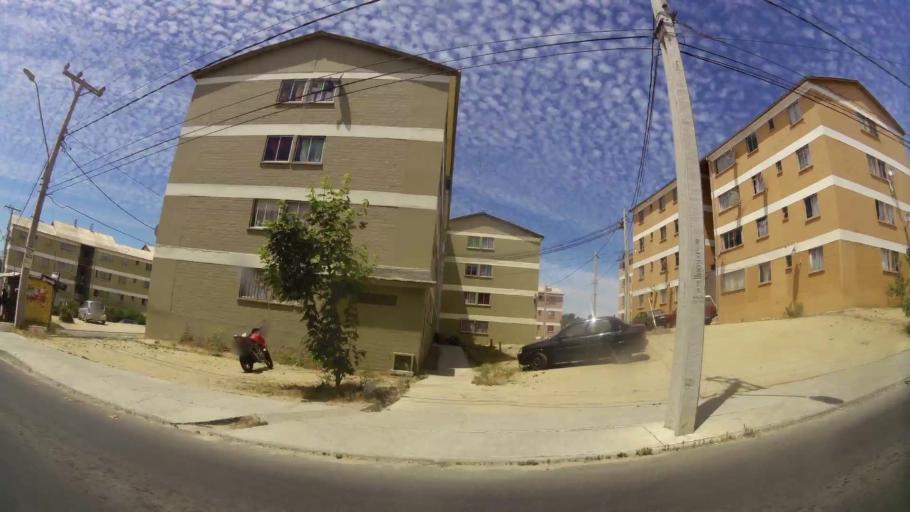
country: CL
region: Valparaiso
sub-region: Provincia de Valparaiso
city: Vina del Mar
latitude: -33.0637
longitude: -71.5644
